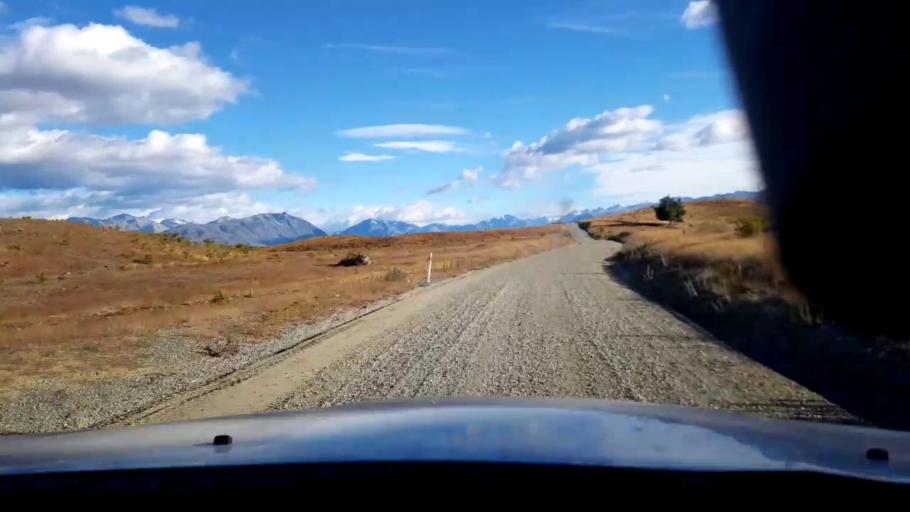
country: NZ
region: Canterbury
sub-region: Timaru District
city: Pleasant Point
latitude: -43.9765
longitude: 170.5111
